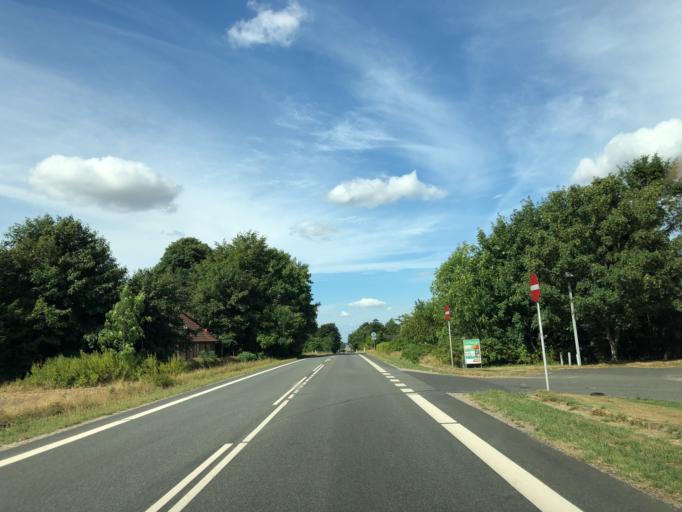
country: DK
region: Central Jutland
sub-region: Ikast-Brande Kommune
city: Bording Kirkeby
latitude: 56.1401
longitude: 9.2853
